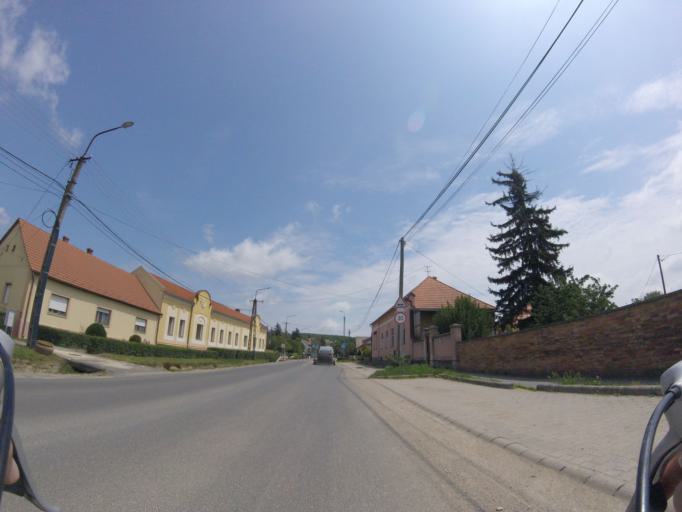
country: HU
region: Baranya
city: Boly
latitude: 45.9970
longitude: 18.4537
